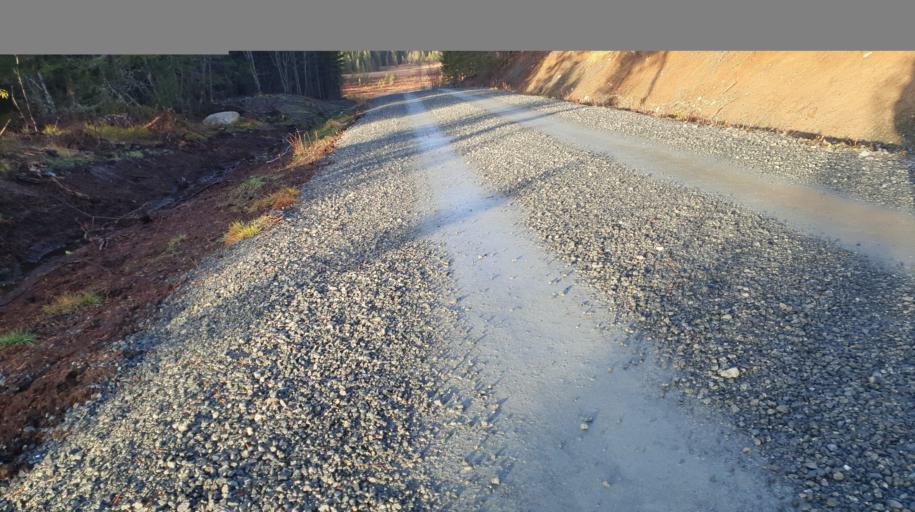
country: NO
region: Sor-Trondelag
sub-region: Melhus
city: Melhus
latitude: 63.3728
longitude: 10.2890
